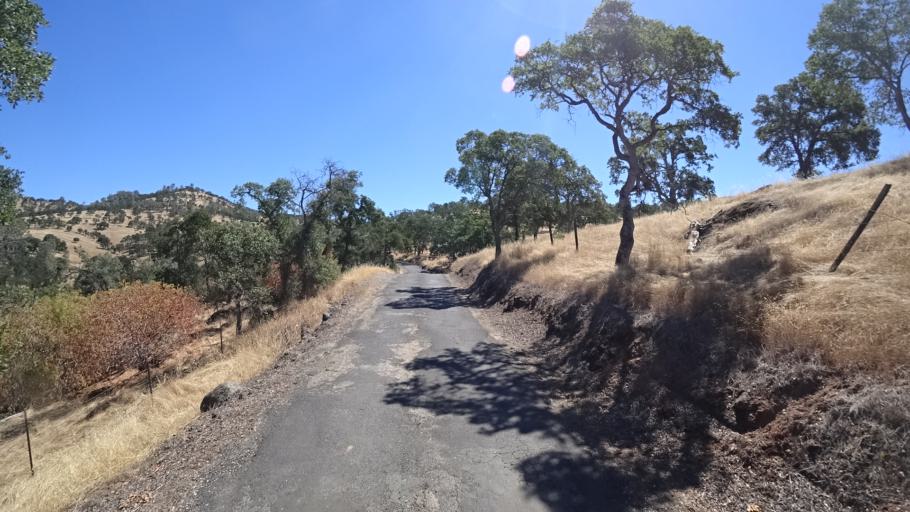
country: US
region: California
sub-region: Calaveras County
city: Rancho Calaveras
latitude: 38.0199
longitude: -120.7860
